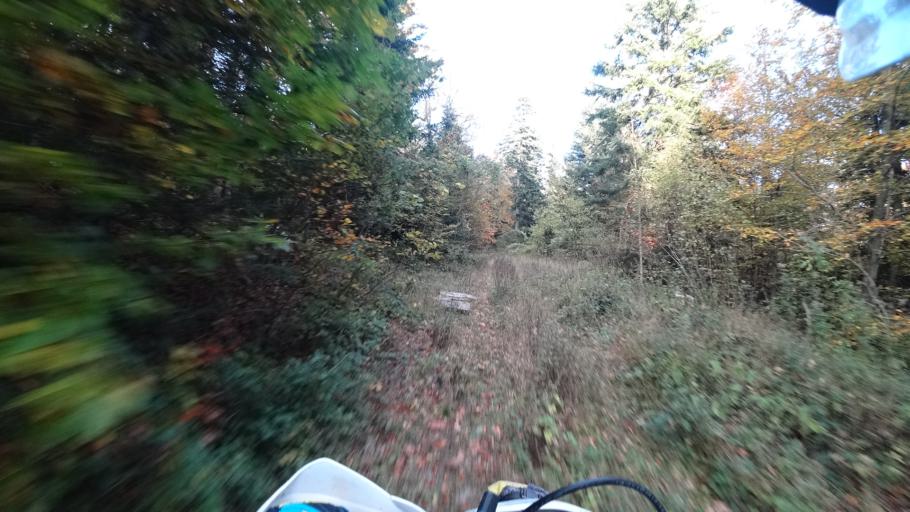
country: HR
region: Karlovacka
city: Plaski
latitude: 45.0341
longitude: 15.4327
